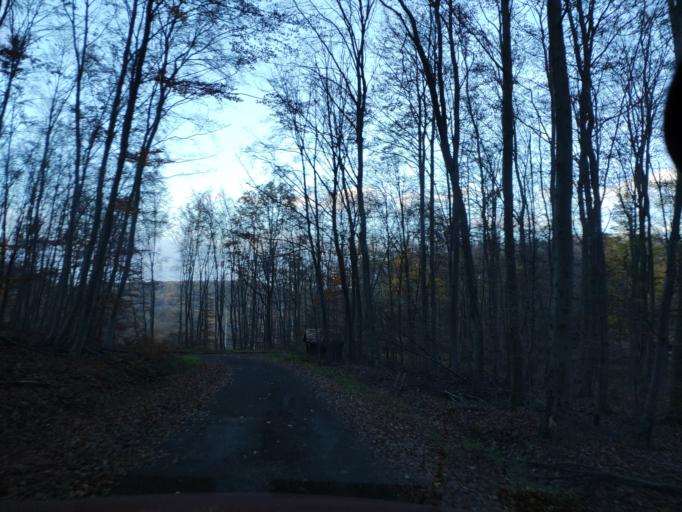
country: SK
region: Kosicky
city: Secovce
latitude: 48.5950
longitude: 21.5111
